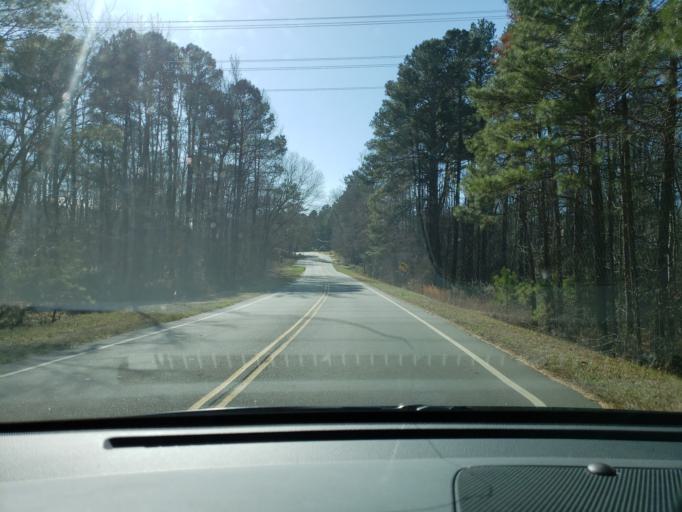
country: US
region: North Carolina
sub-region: Orange County
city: Chapel Hill
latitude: 35.9583
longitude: -79.0140
